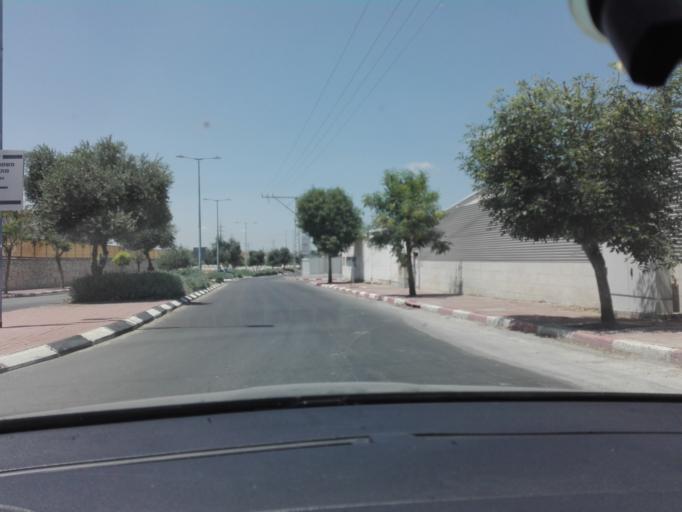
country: IL
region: Southern District
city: Qiryat Gat
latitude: 31.5946
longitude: 34.7790
